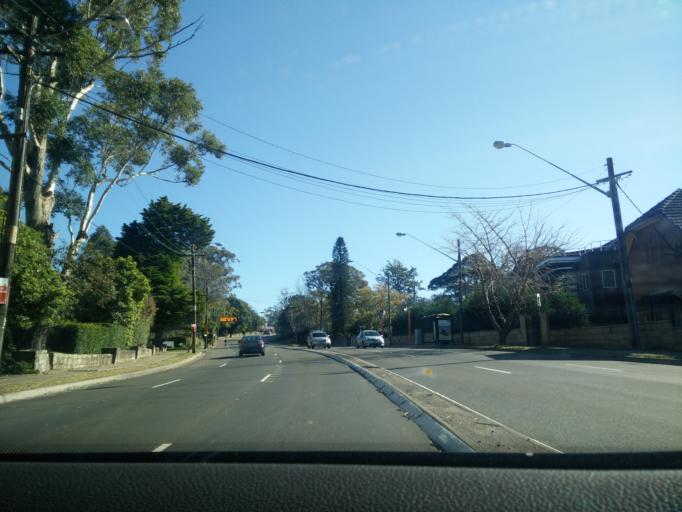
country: AU
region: New South Wales
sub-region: Ku-ring-gai
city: North Wahroonga
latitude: -33.7228
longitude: 151.1185
